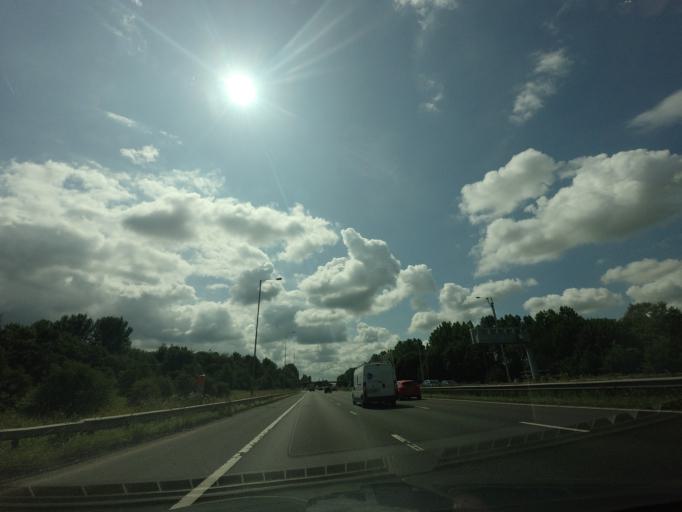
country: GB
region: England
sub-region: Lancashire
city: Clayton-le-Woods
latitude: 53.6946
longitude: -2.6774
